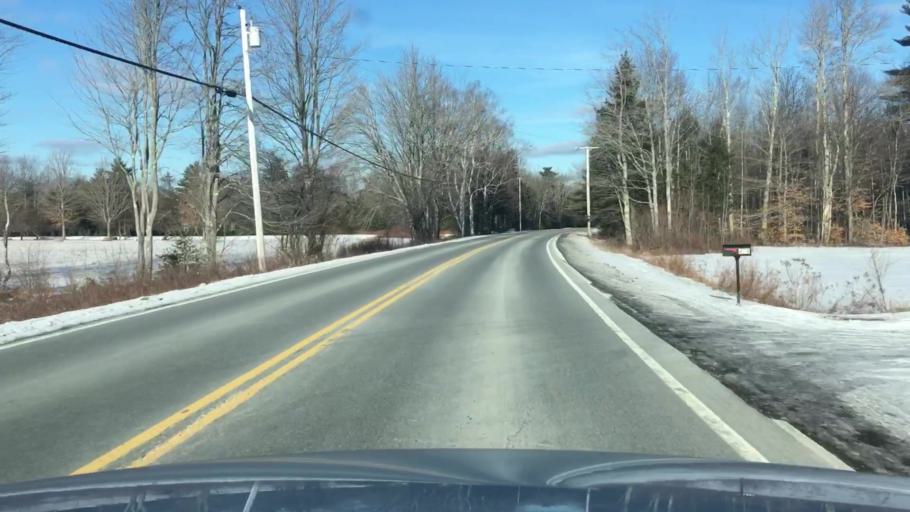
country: US
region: Maine
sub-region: Penobscot County
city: Holden
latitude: 44.7658
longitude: -68.5939
